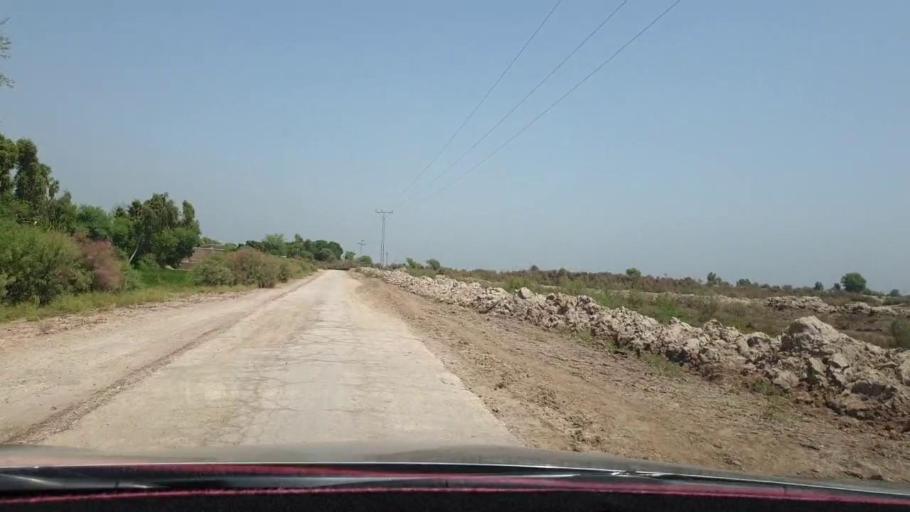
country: PK
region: Sindh
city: Warah
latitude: 27.4344
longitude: 67.7177
